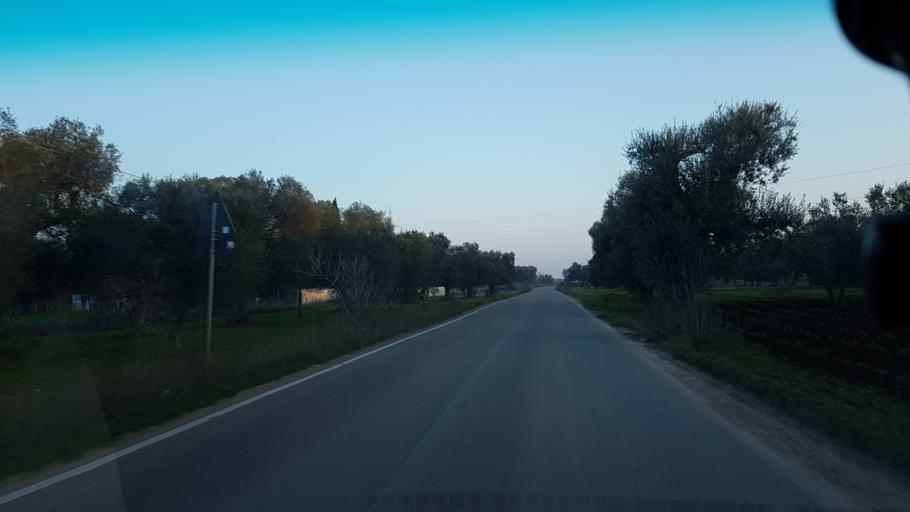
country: IT
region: Apulia
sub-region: Provincia di Brindisi
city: San Vito dei Normanni
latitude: 40.6398
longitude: 17.7795
